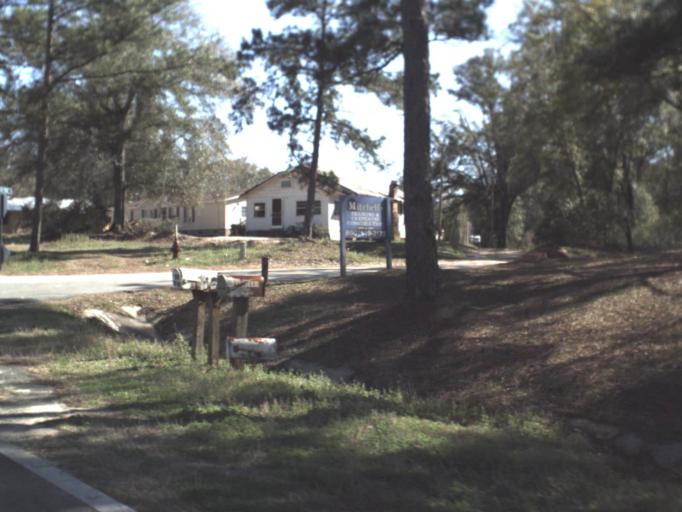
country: US
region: Florida
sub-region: Gadsden County
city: Quincy
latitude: 30.5584
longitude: -84.5341
